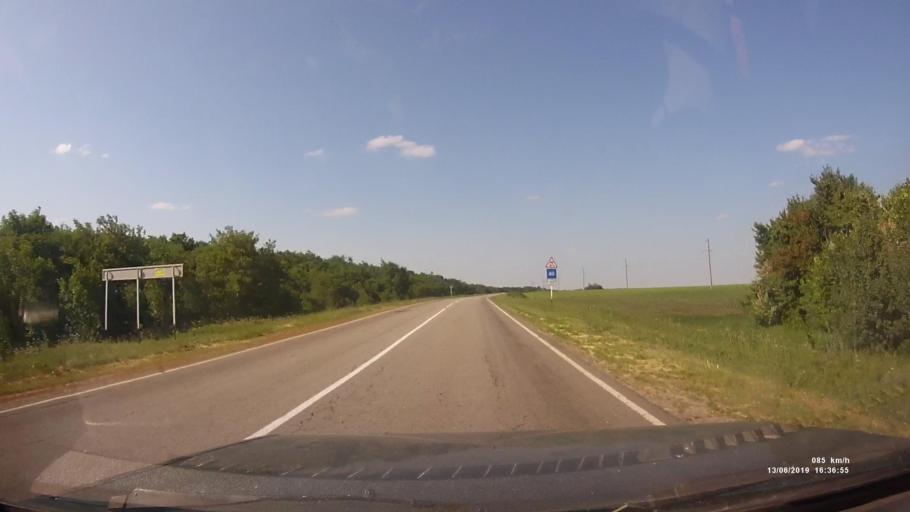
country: RU
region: Rostov
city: Kazanskaya
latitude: 49.9008
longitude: 41.3089
